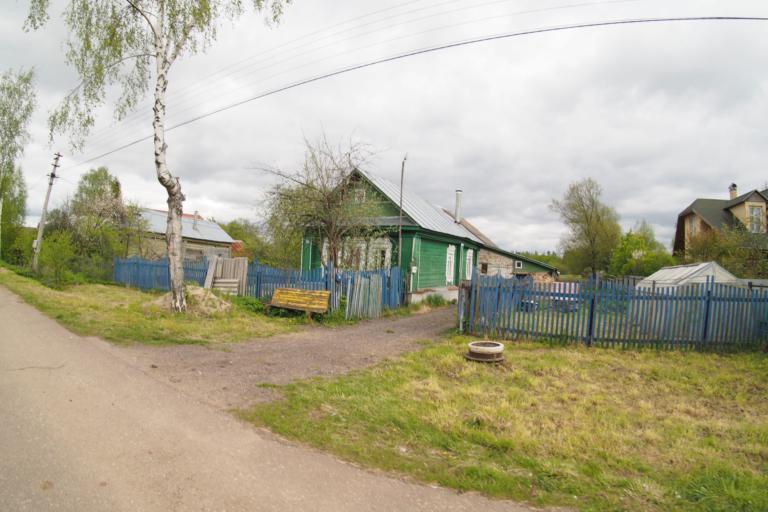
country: RU
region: Moskovskaya
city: Rechitsy
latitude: 55.5715
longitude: 38.4872
